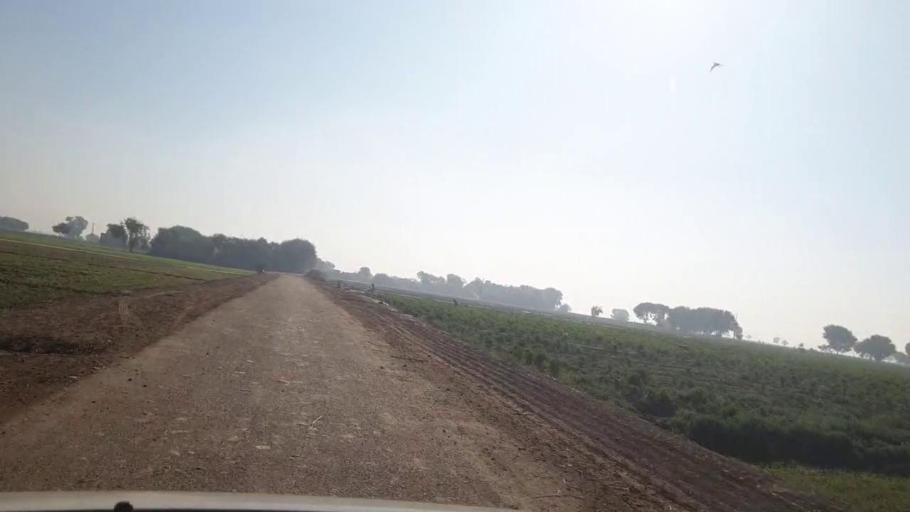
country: PK
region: Sindh
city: Dadu
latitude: 26.6382
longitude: 67.8326
